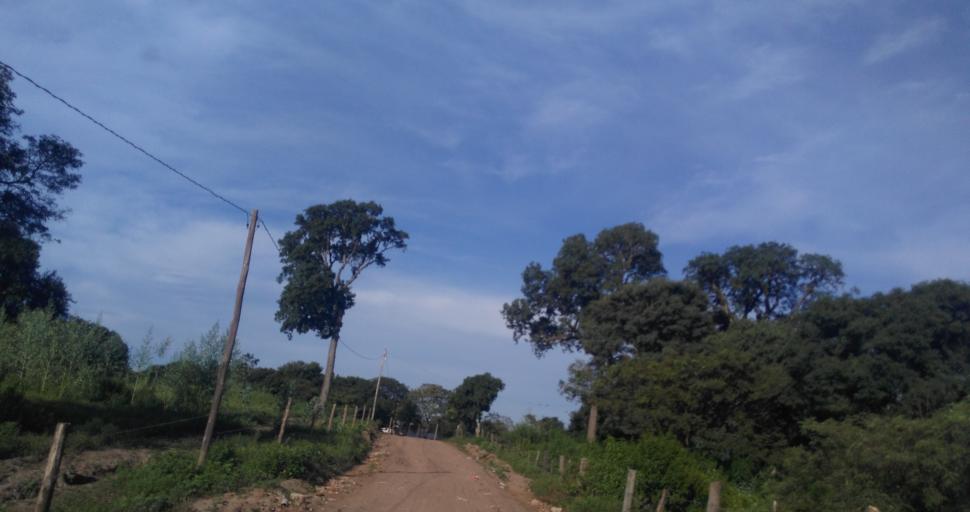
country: AR
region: Chaco
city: Fontana
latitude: -27.4102
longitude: -59.0234
